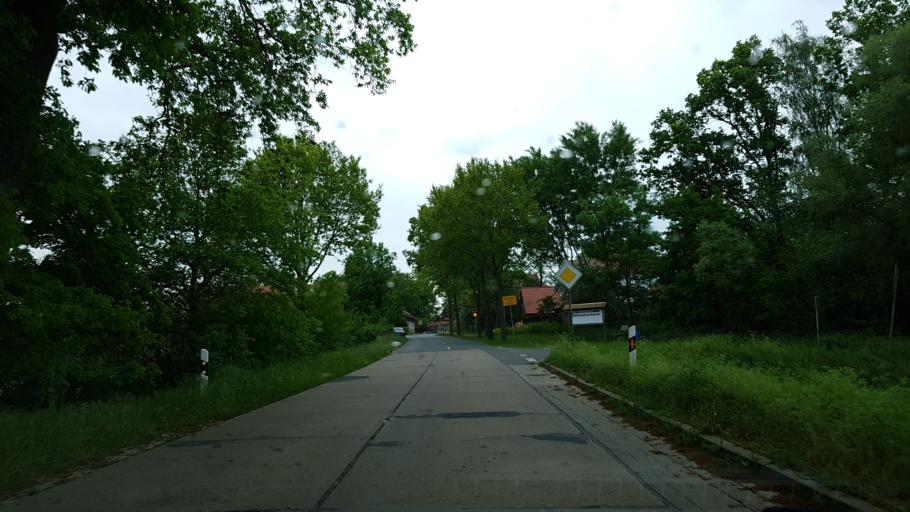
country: DE
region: Lower Saxony
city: Gartow
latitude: 53.0529
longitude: 11.4350
